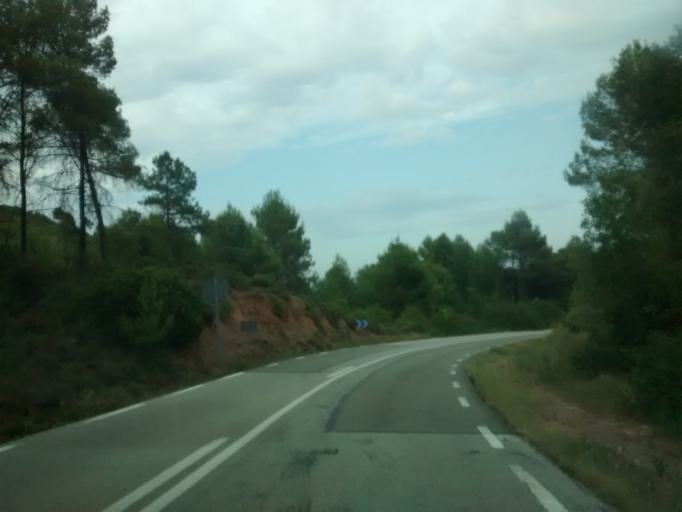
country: ES
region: Catalonia
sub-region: Provincia de Barcelona
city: Rajadell
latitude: 41.7632
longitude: 1.7181
